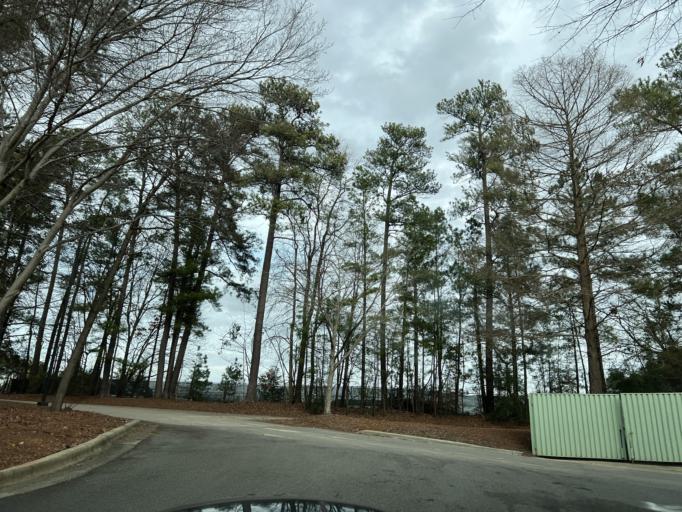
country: US
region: North Carolina
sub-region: Wake County
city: West Raleigh
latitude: 35.7677
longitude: -78.7159
